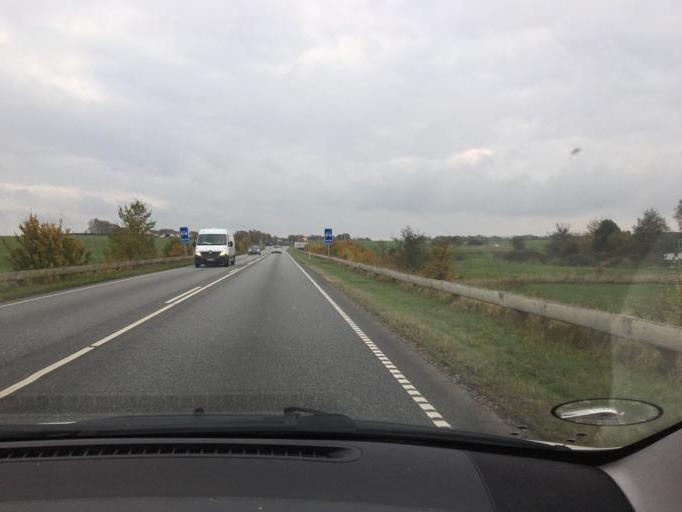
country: DK
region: South Denmark
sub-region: Fredericia Kommune
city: Fredericia
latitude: 55.6112
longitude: 9.7529
